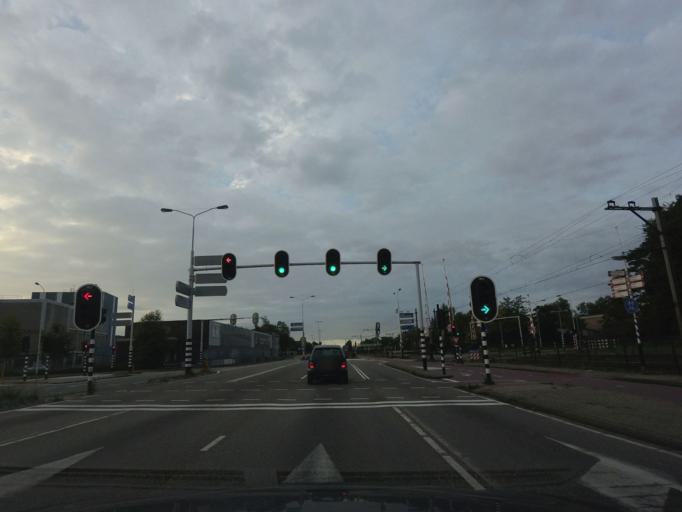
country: NL
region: North Holland
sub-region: Gemeente Zaanstad
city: Zaanstad
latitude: 52.4712
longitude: 4.8053
